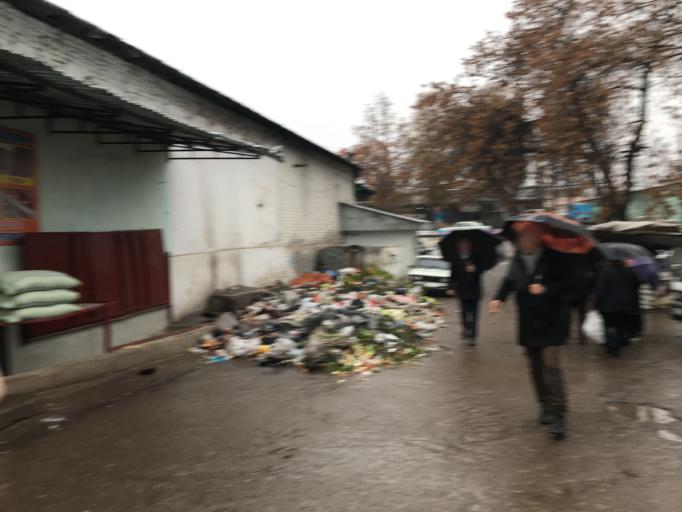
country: UZ
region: Toshkent
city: Yangiyul
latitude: 41.1174
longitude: 69.0534
